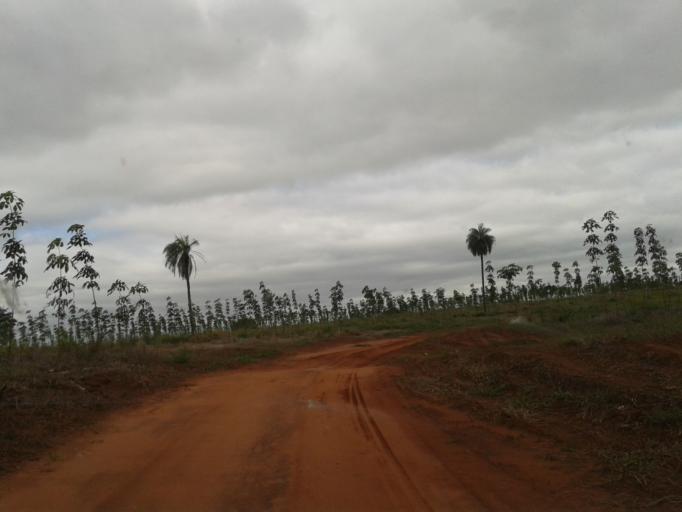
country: BR
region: Minas Gerais
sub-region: Campina Verde
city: Campina Verde
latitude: -19.5172
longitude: -49.6286
